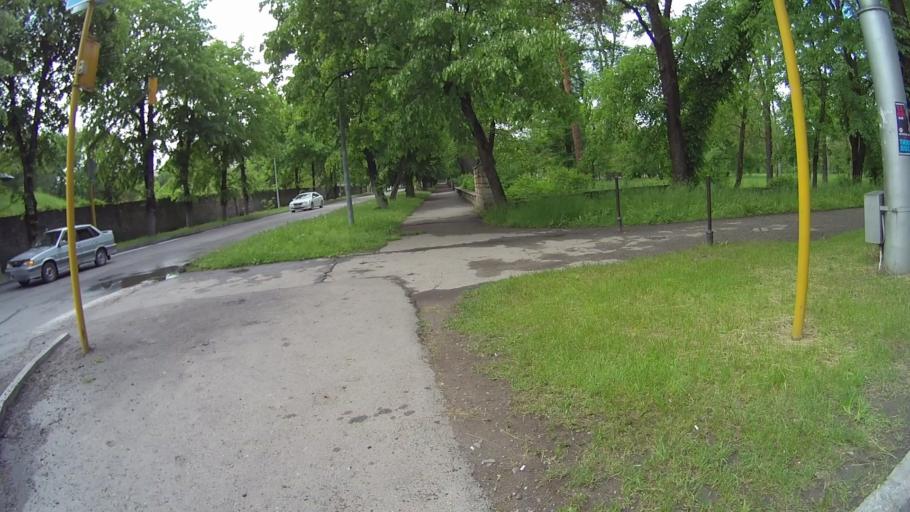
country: RU
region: Kabardino-Balkariya
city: Vol'nyy Aul
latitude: 43.4656
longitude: 43.5902
